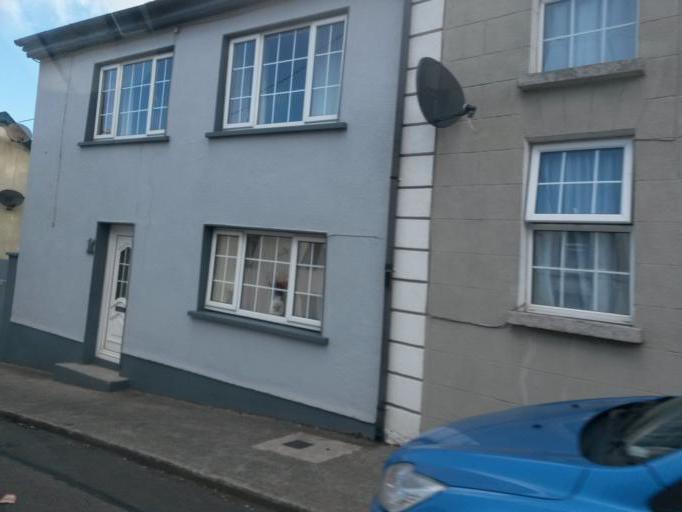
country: IE
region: Leinster
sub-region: Loch Garman
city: Enniscorthy
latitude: 52.5028
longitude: -6.5632
